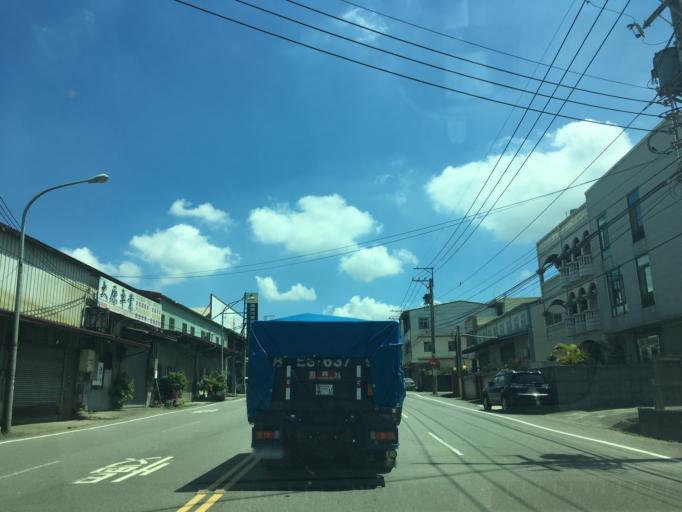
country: TW
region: Taiwan
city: Fengyuan
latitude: 24.2160
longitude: 120.7235
